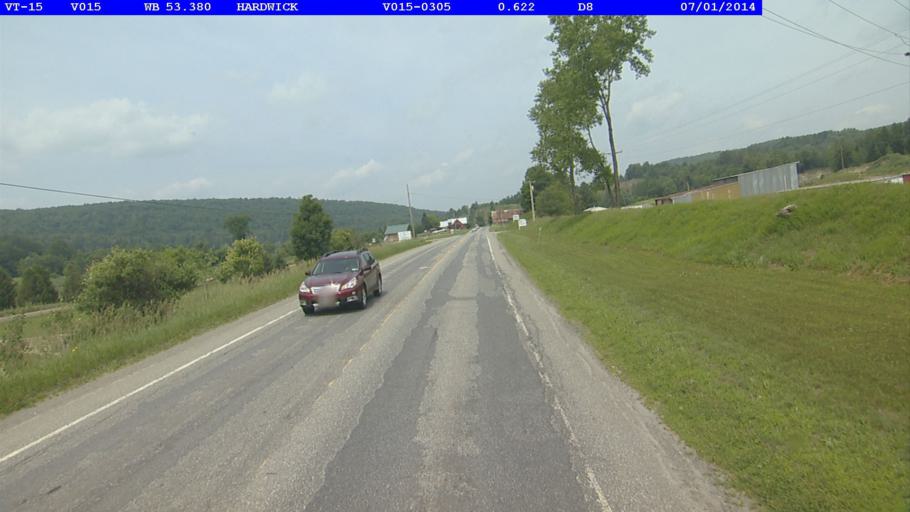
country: US
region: Vermont
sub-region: Caledonia County
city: Hardwick
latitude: 44.5196
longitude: -72.4093
